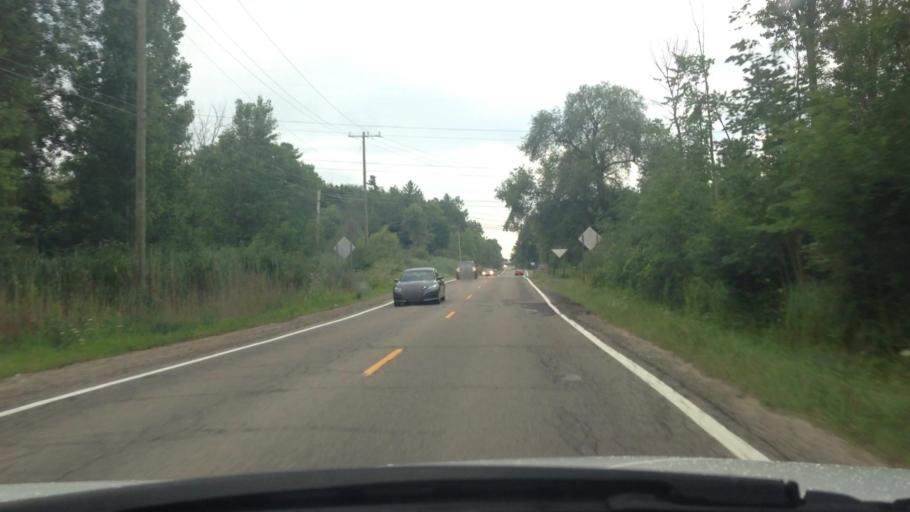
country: US
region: Michigan
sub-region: Oakland County
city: Clarkston
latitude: 42.7329
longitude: -83.3499
